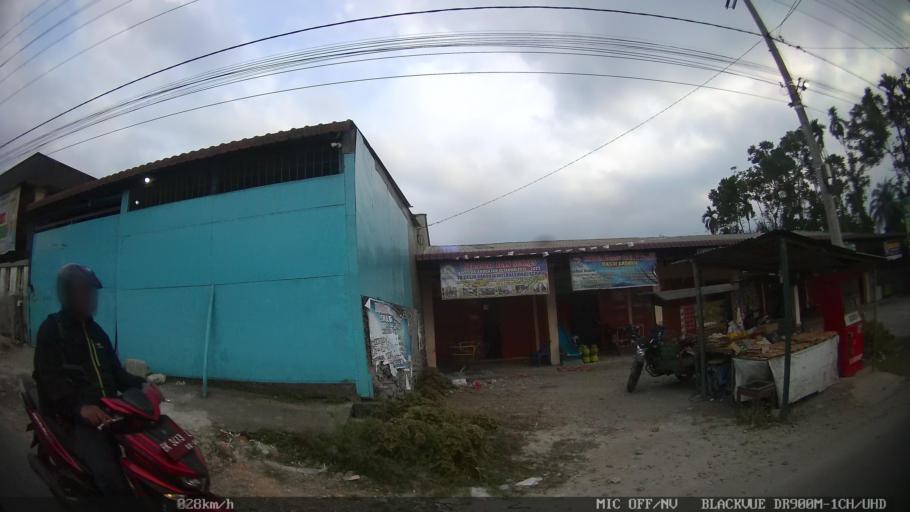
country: ID
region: North Sumatra
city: Sunggal
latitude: 3.5610
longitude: 98.5734
